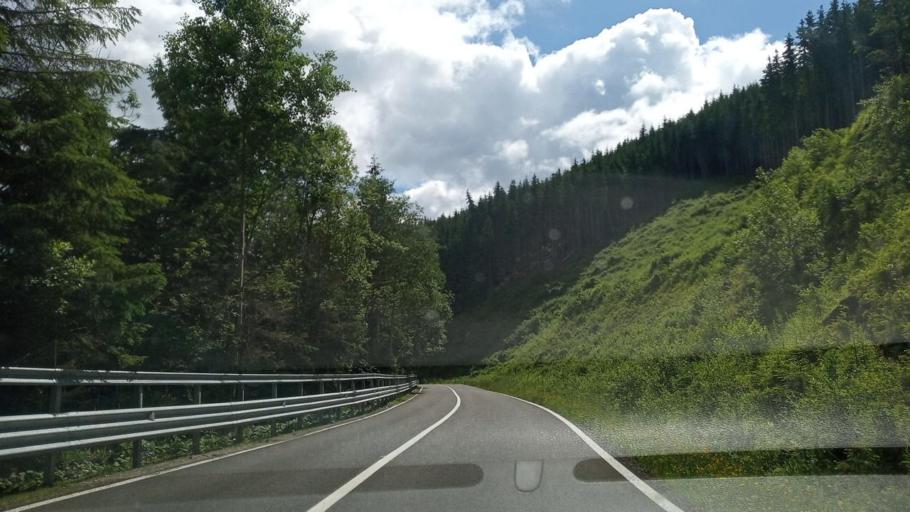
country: RO
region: Alba
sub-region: Comuna Sugag
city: Sugag
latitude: 45.5853
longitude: 23.6257
